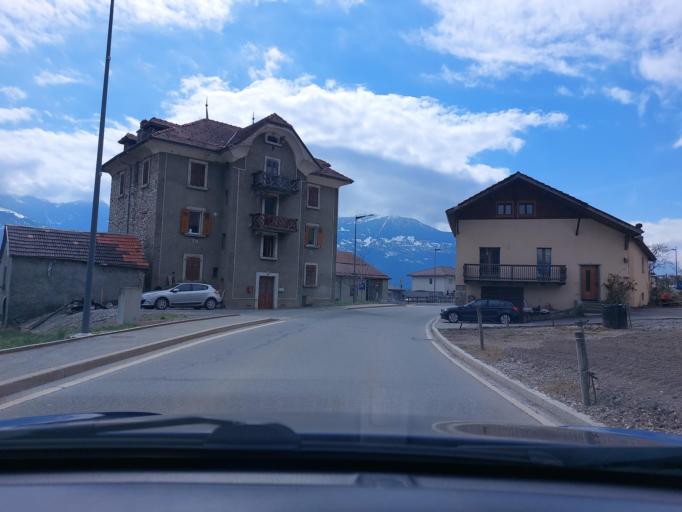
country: CH
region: Valais
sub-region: Conthey District
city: Conthey
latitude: 46.2412
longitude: 7.2958
